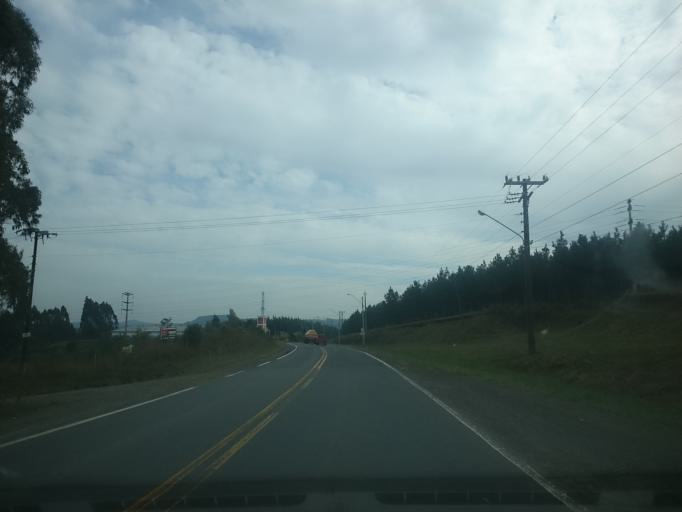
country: BR
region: Santa Catarina
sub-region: Lages
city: Lages
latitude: -27.7573
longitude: -50.3298
